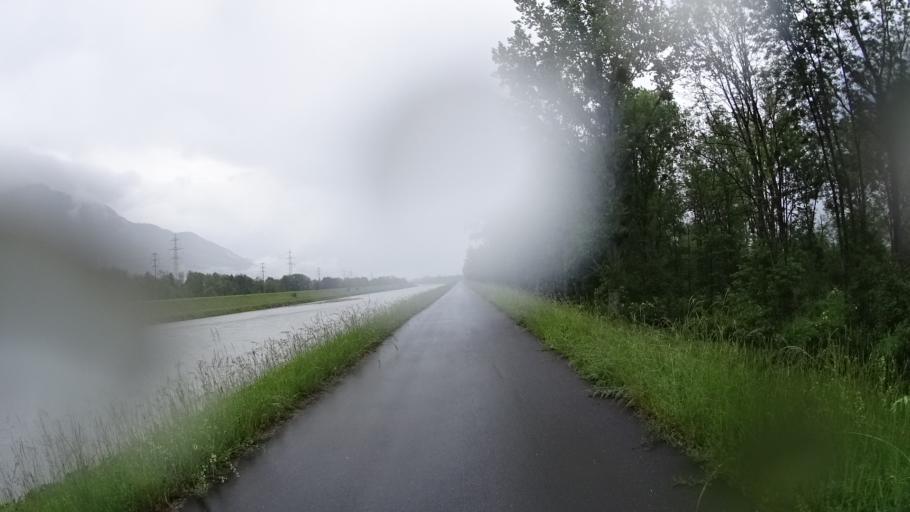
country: LI
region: Gamprin
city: Gamprin
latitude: 47.2297
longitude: 9.5097
